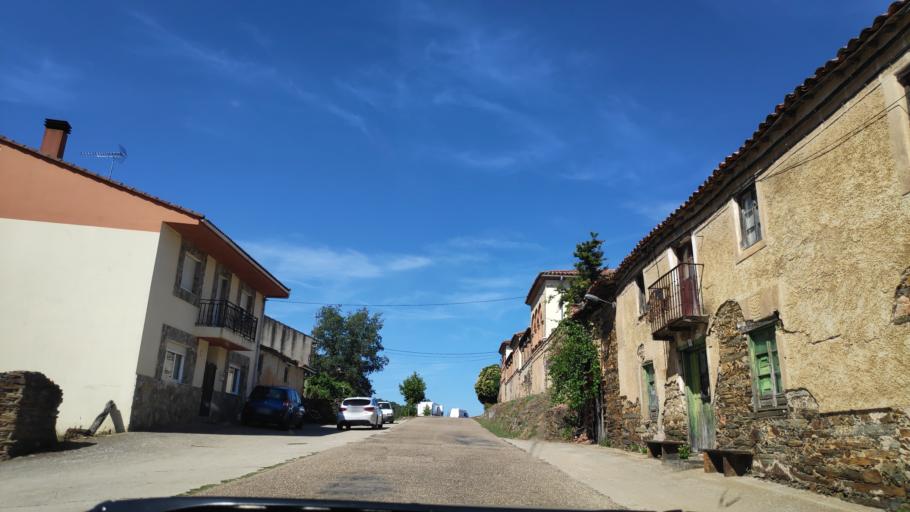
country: ES
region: Castille and Leon
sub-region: Provincia de Zamora
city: Rabano de Aliste
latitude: 41.7297
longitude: -6.4563
